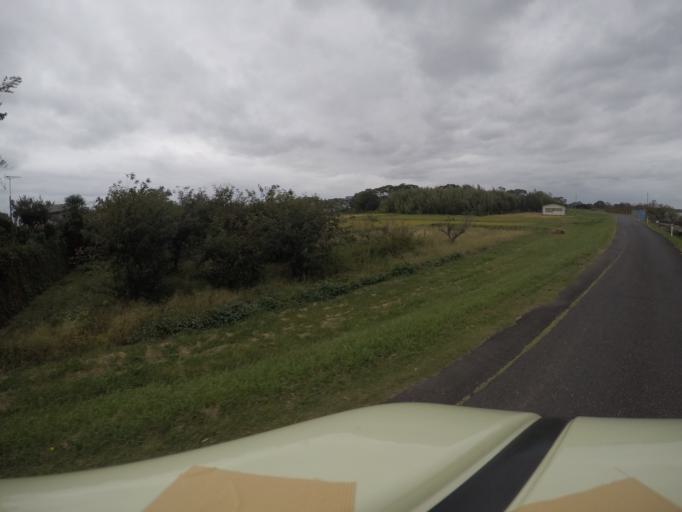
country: JP
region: Ibaraki
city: Inashiki
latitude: 35.9827
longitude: 140.3814
